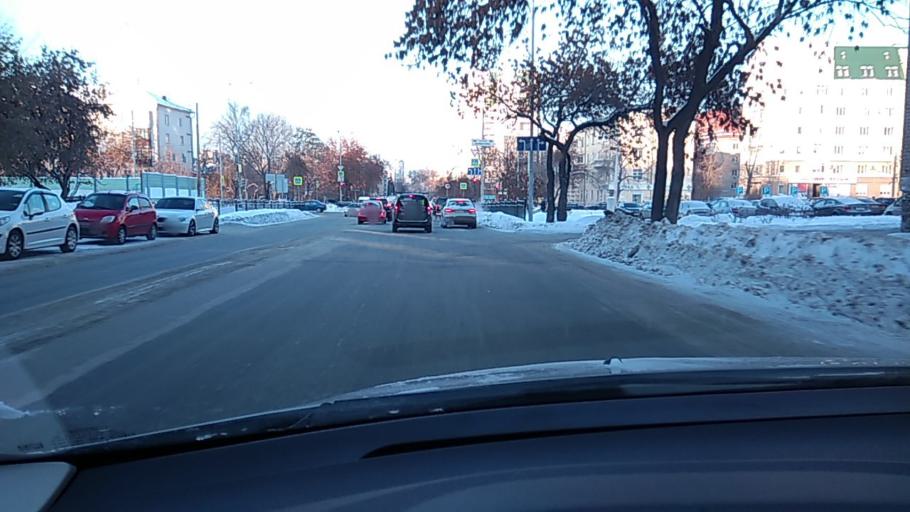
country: RU
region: Sverdlovsk
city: Yekaterinburg
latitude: 56.8152
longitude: 60.6108
